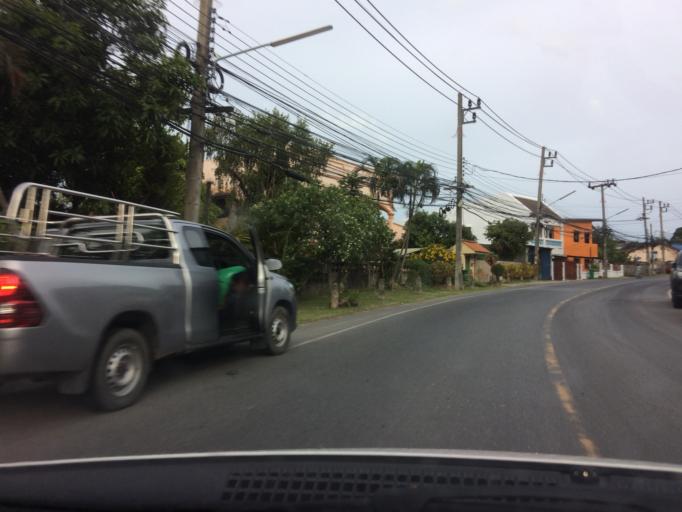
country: TH
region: Phuket
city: Ban Ratsada
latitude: 7.9044
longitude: 98.4092
